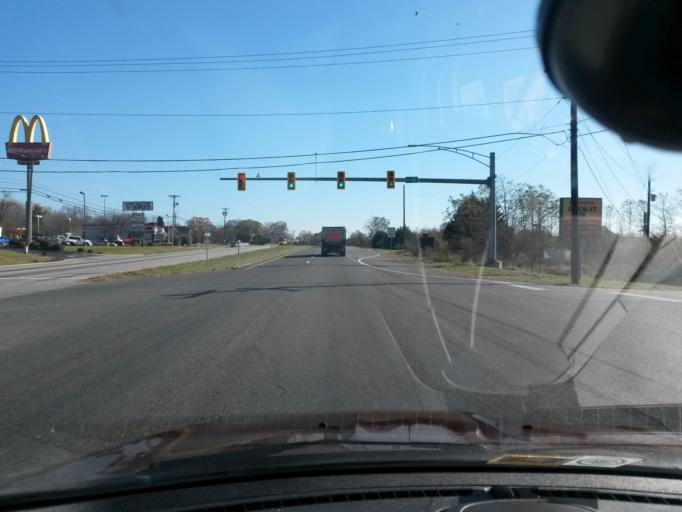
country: US
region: Virginia
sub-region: City of Bedford
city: Bedford
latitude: 37.3236
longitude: -79.4973
